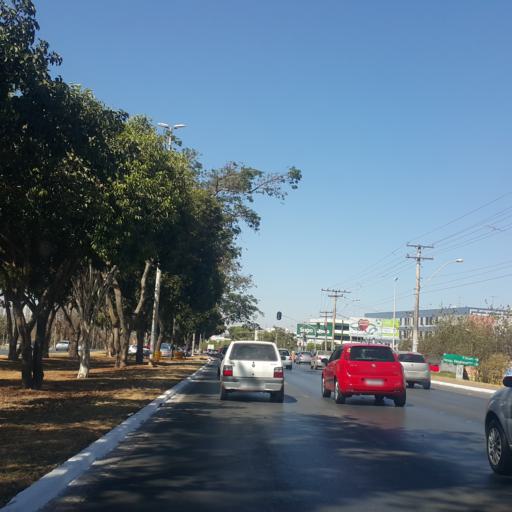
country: BR
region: Federal District
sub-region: Brasilia
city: Brasilia
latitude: -15.8149
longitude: -48.0584
